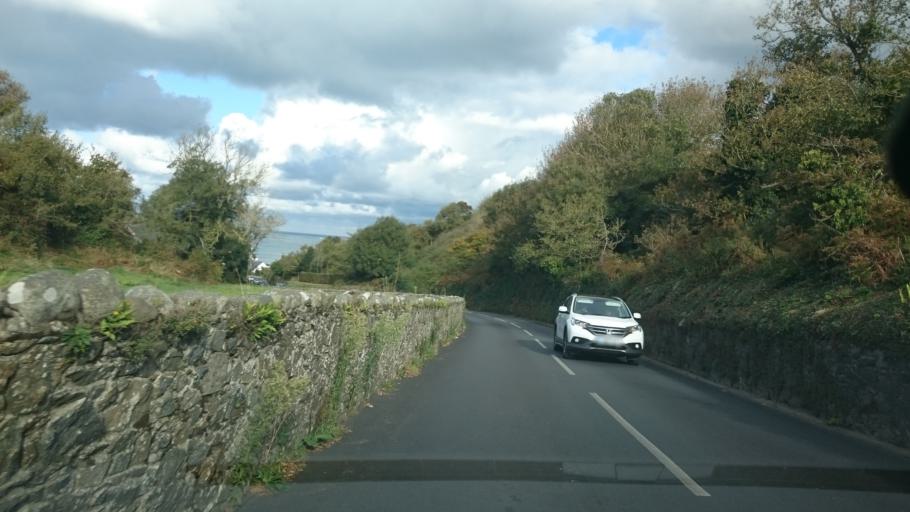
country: GG
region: St Peter Port
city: Saint Peter Port
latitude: 49.4314
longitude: -2.6581
